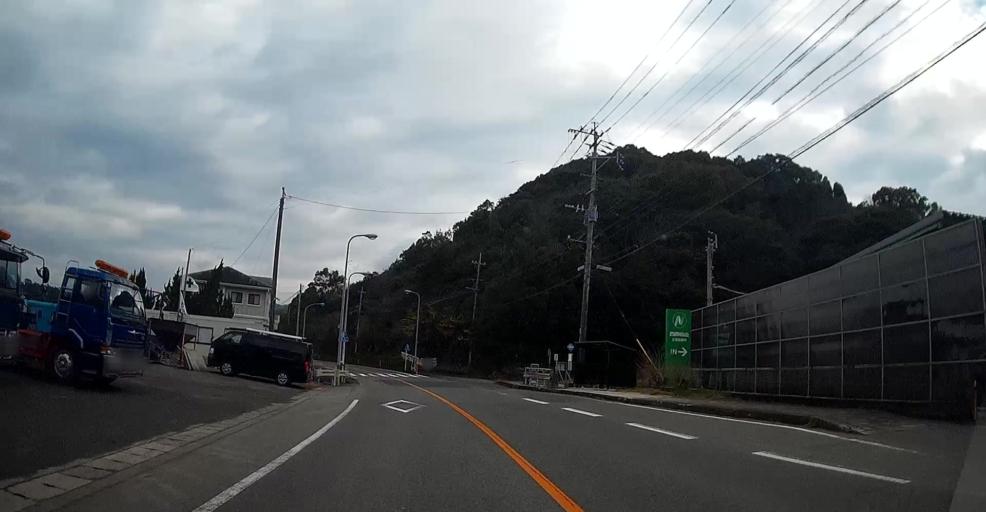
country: JP
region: Kumamoto
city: Hondo
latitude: 32.4568
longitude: 130.2207
